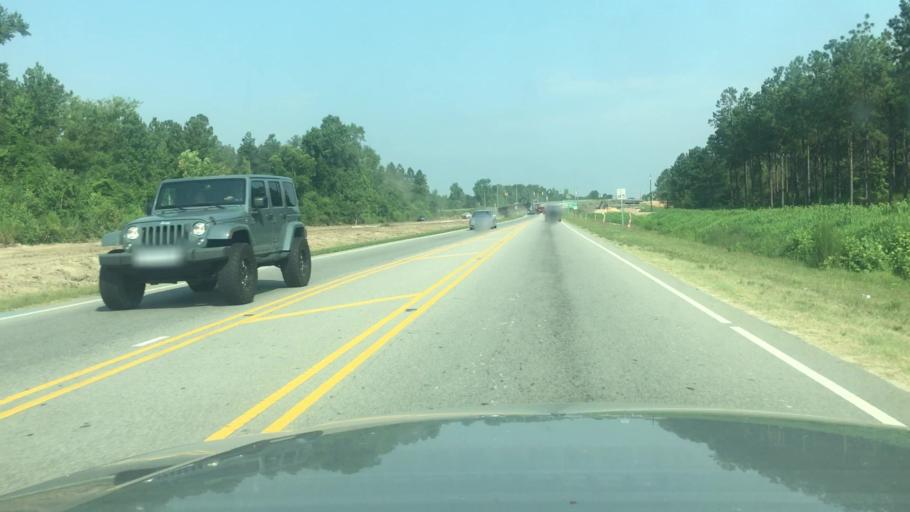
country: US
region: North Carolina
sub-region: Cumberland County
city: Hope Mills
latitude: 34.9419
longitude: -78.9267
